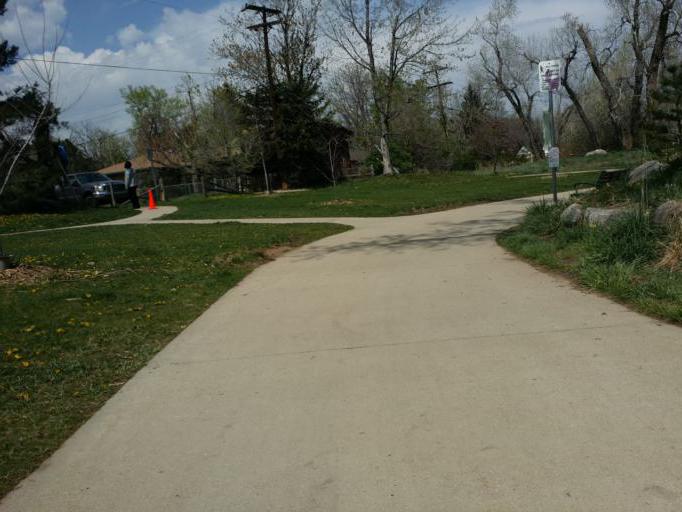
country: US
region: Colorado
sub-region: Boulder County
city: Boulder
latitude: 39.9896
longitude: -105.2505
